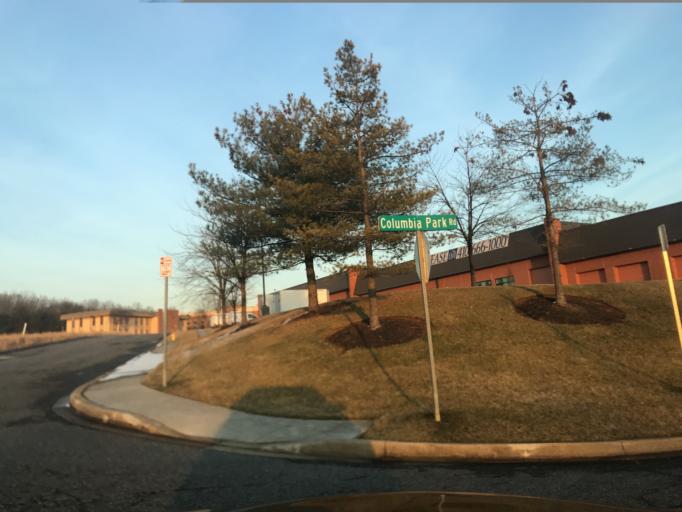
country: US
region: Maryland
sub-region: Harford County
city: Edgewood
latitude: 39.4527
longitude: -76.3141
